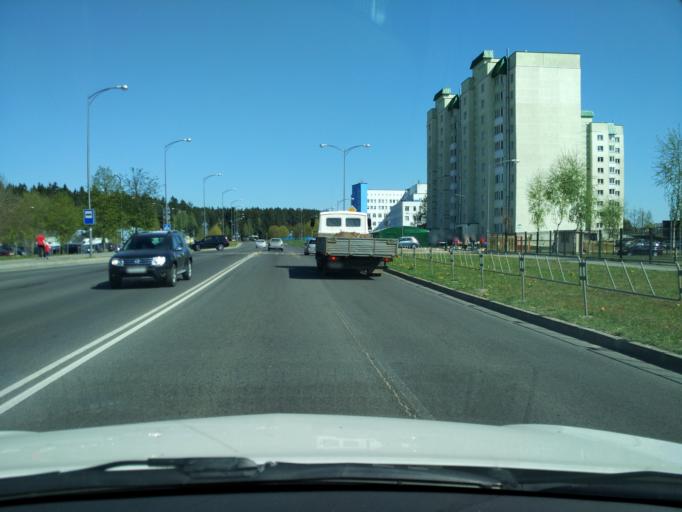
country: BY
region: Minsk
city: Borovlyany
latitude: 53.9987
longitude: 27.6860
